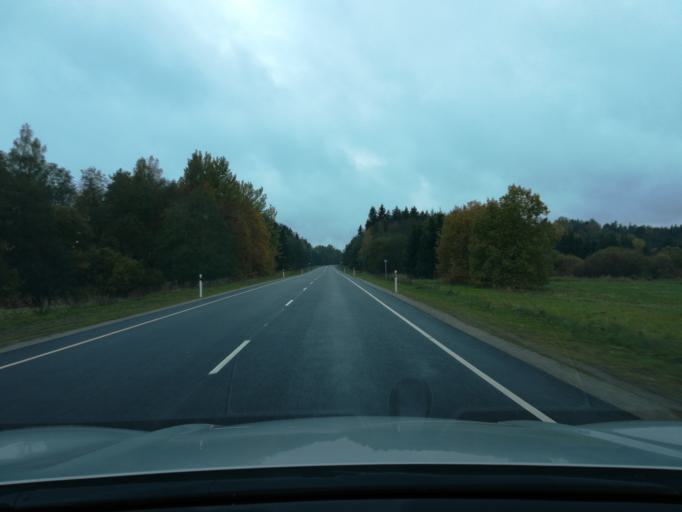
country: EE
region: Ida-Virumaa
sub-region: Johvi vald
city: Johvi
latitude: 59.1421
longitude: 27.3530
